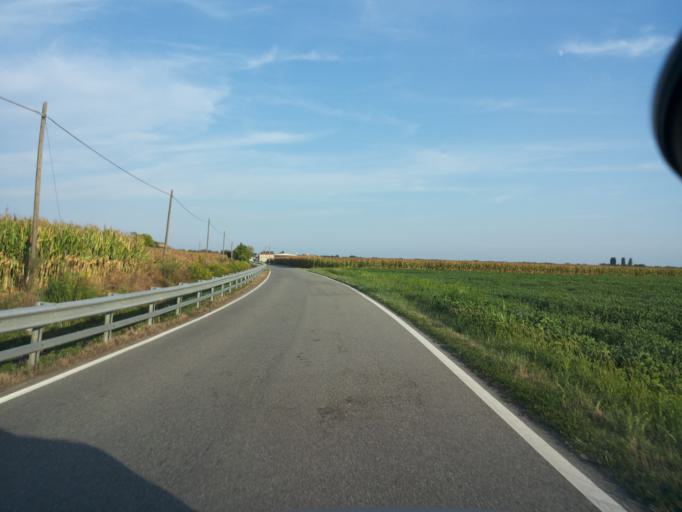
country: IT
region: Piedmont
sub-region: Provincia di Vercelli
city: Crova
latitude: 45.3369
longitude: 8.1957
